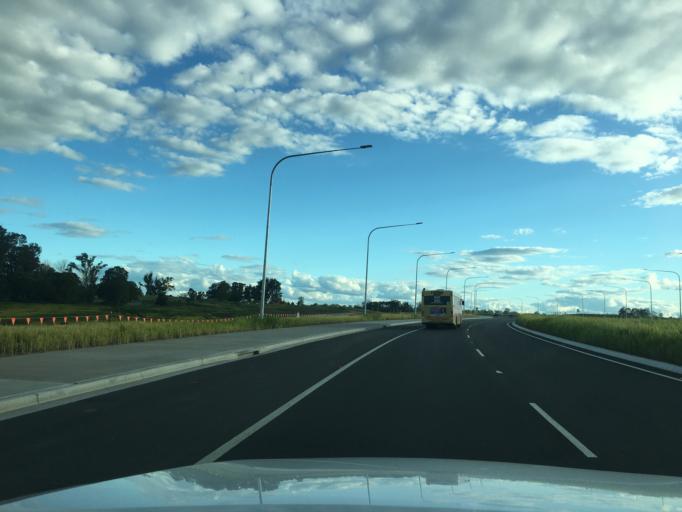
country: AU
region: New South Wales
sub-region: Liverpool
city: Bringelly
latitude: -33.8767
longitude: 150.7488
